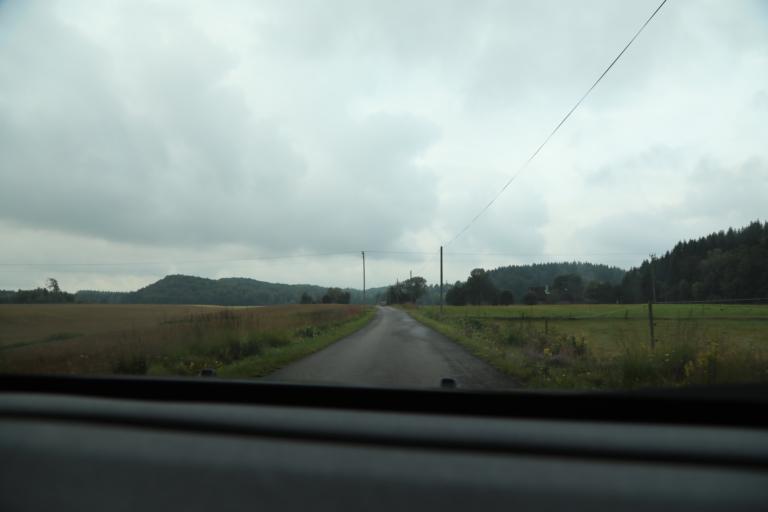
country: SE
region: Halland
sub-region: Falkenbergs Kommun
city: Falkenberg
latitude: 57.1116
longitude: 12.6785
